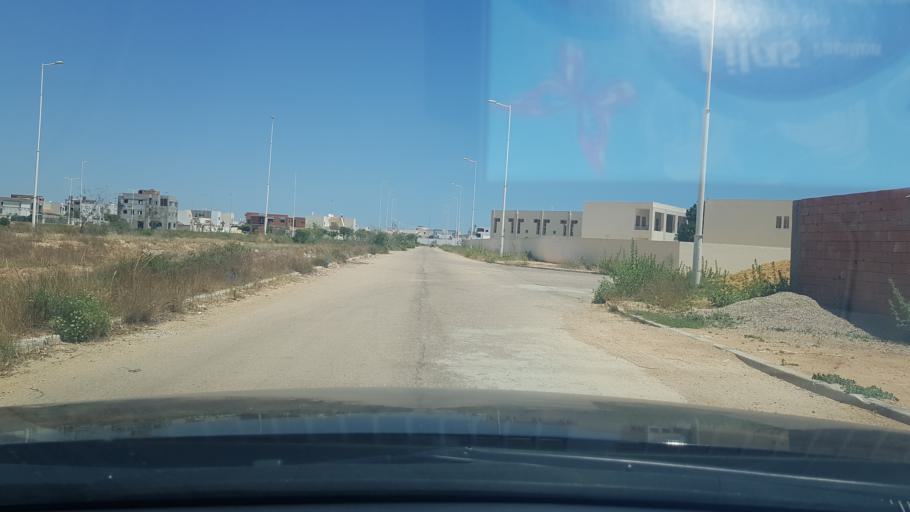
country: TN
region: Safaqis
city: Al Qarmadah
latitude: 34.8364
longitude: 10.7576
